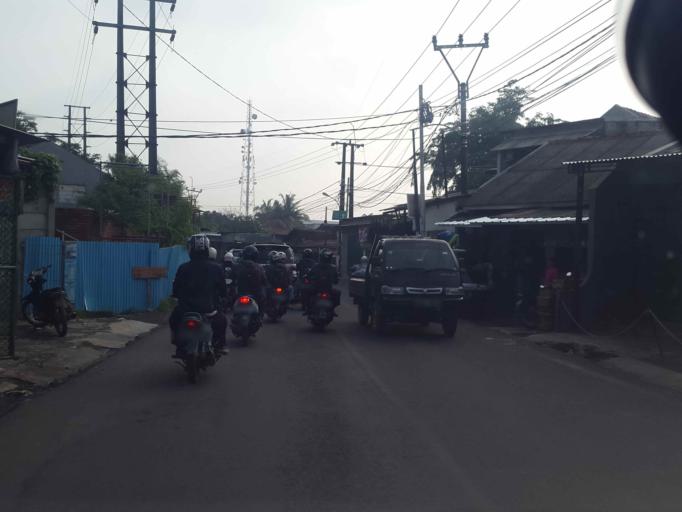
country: ID
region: West Java
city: Bekasi
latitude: -6.2822
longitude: 107.0371
